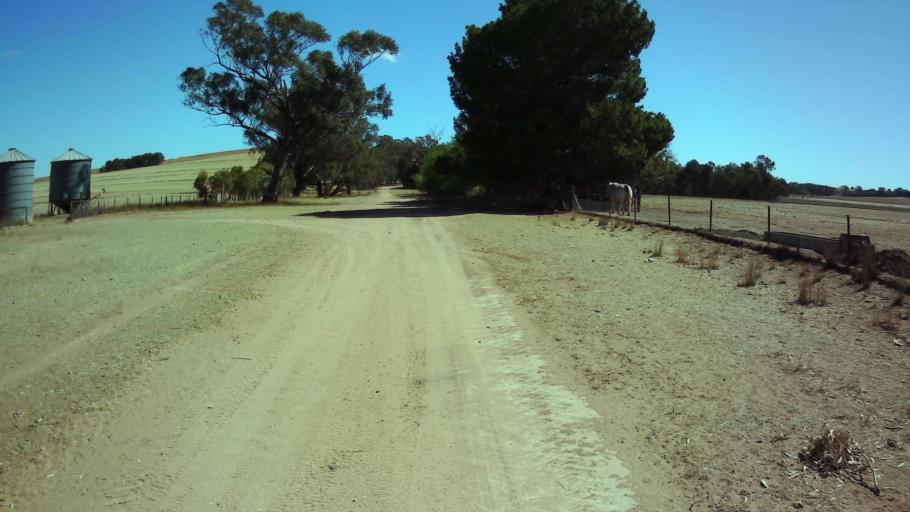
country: AU
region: New South Wales
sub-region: Weddin
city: Grenfell
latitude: -34.0040
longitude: 148.4360
